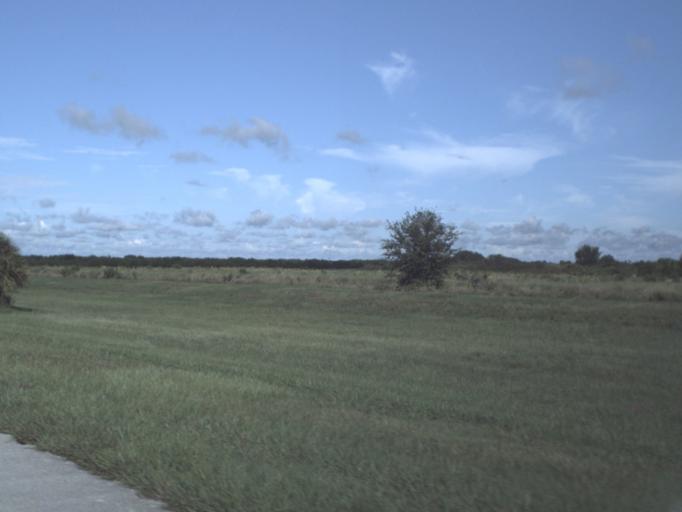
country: US
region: Florida
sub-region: Highlands County
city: Placid Lakes
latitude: 27.2097
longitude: -81.5881
